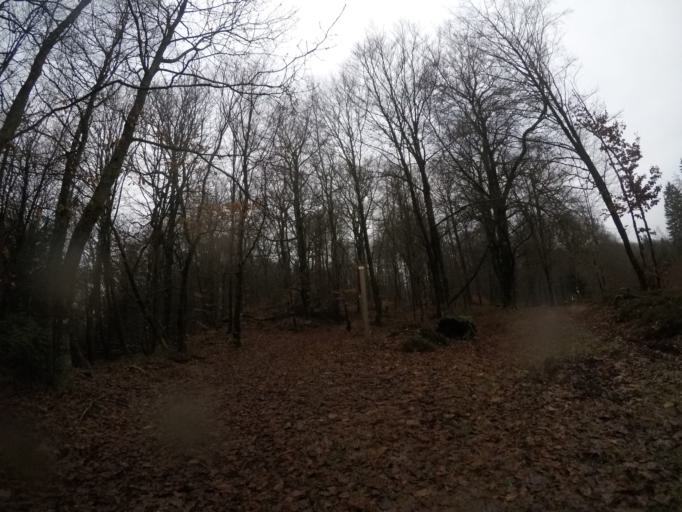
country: BE
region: Wallonia
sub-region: Province du Luxembourg
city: Fauvillers
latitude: 49.8100
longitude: 5.6188
